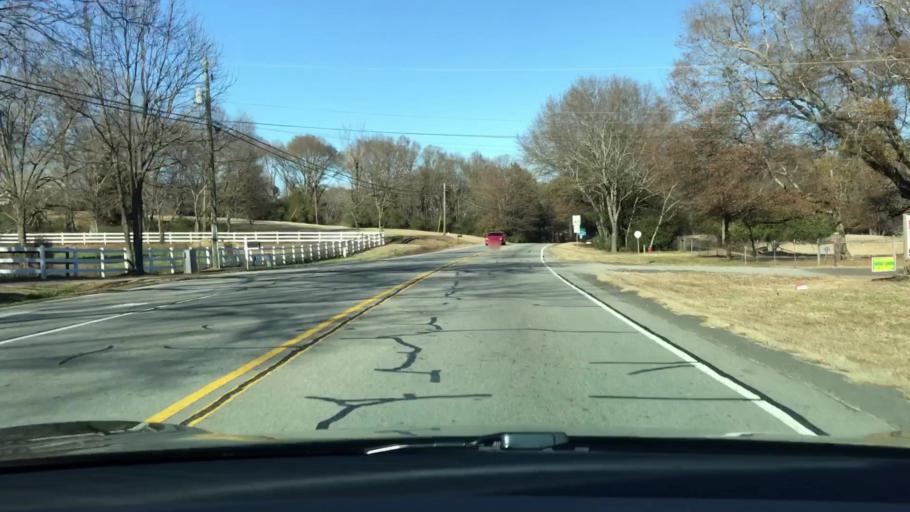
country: US
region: Georgia
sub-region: Barrow County
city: Russell
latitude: 33.9243
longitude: -83.7155
